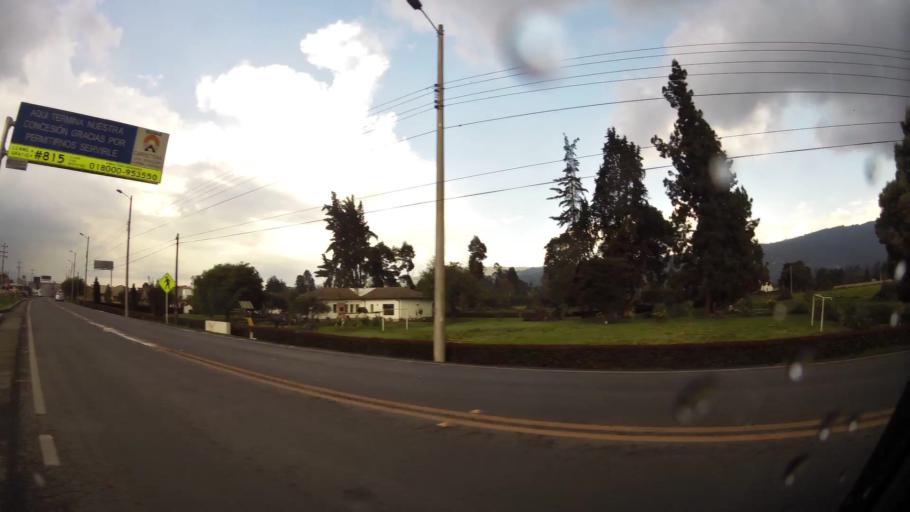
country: CO
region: Cundinamarca
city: Chia
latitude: 4.8599
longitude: -74.0479
